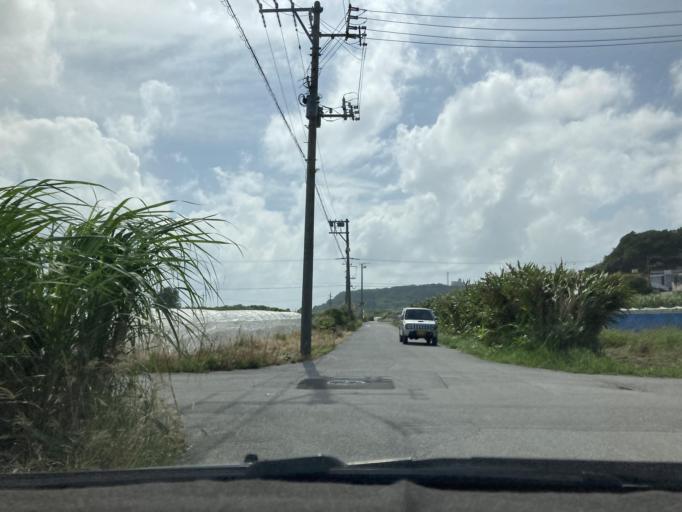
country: JP
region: Okinawa
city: Ginowan
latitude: 26.1505
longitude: 127.8053
